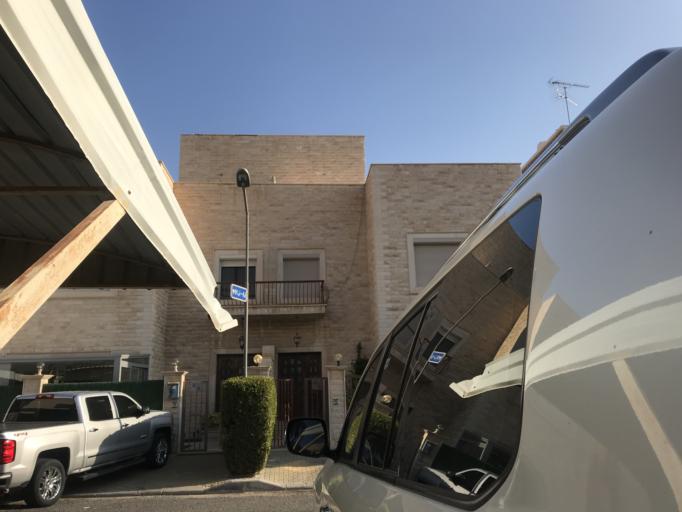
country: KW
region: Al Asimah
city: Ad Dasmah
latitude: 29.3530
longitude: 48.0063
